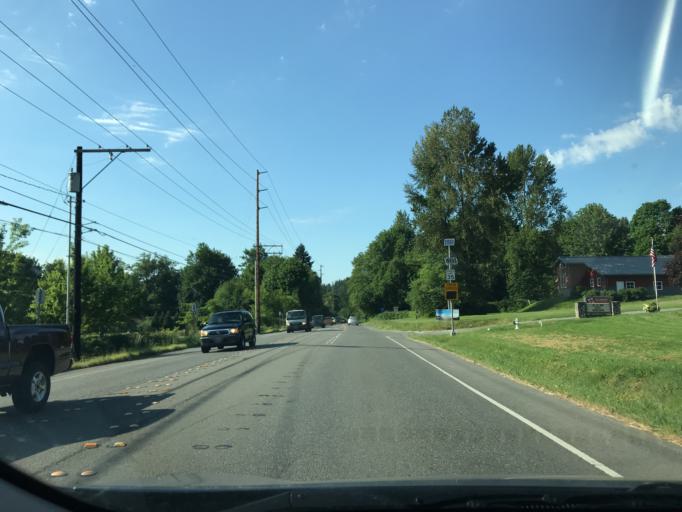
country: US
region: Washington
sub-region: King County
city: Issaquah
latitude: 47.5091
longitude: -122.0231
